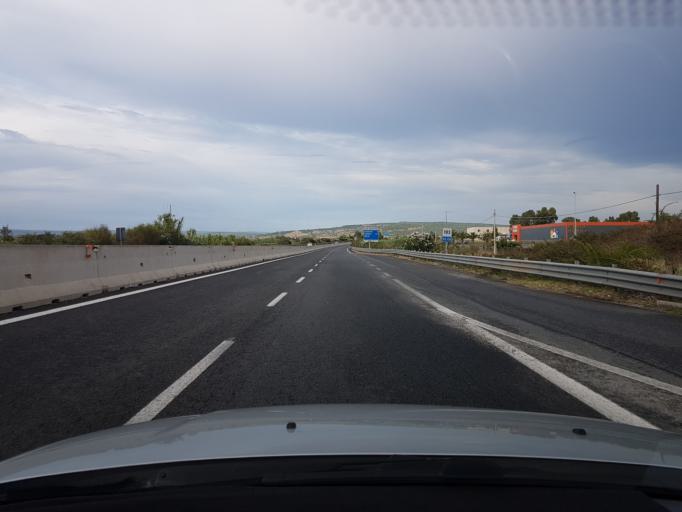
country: IT
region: Sardinia
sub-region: Provincia di Oristano
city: Tramatza
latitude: 39.9905
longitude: 8.6429
